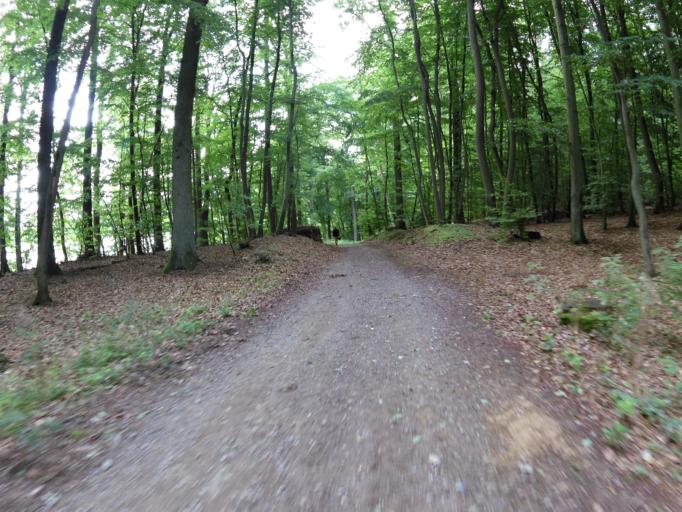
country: DE
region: Mecklenburg-Vorpommern
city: Seebad Bansin
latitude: 53.9581
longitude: 14.1082
